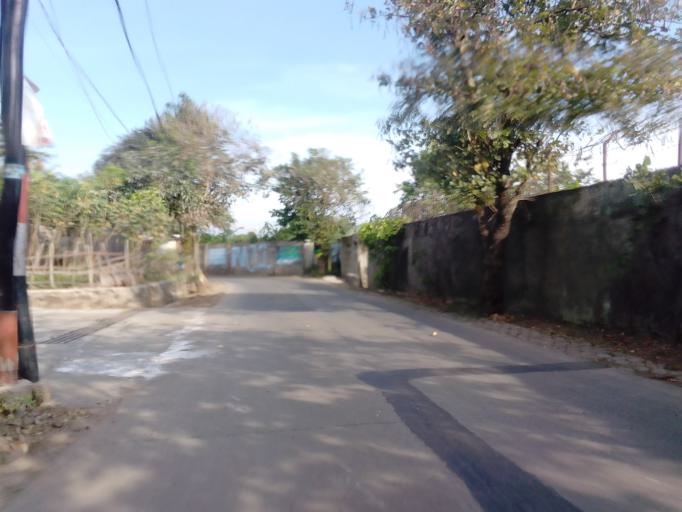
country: ID
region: West Java
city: Cileunyi
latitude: -6.9307
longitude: 107.7050
